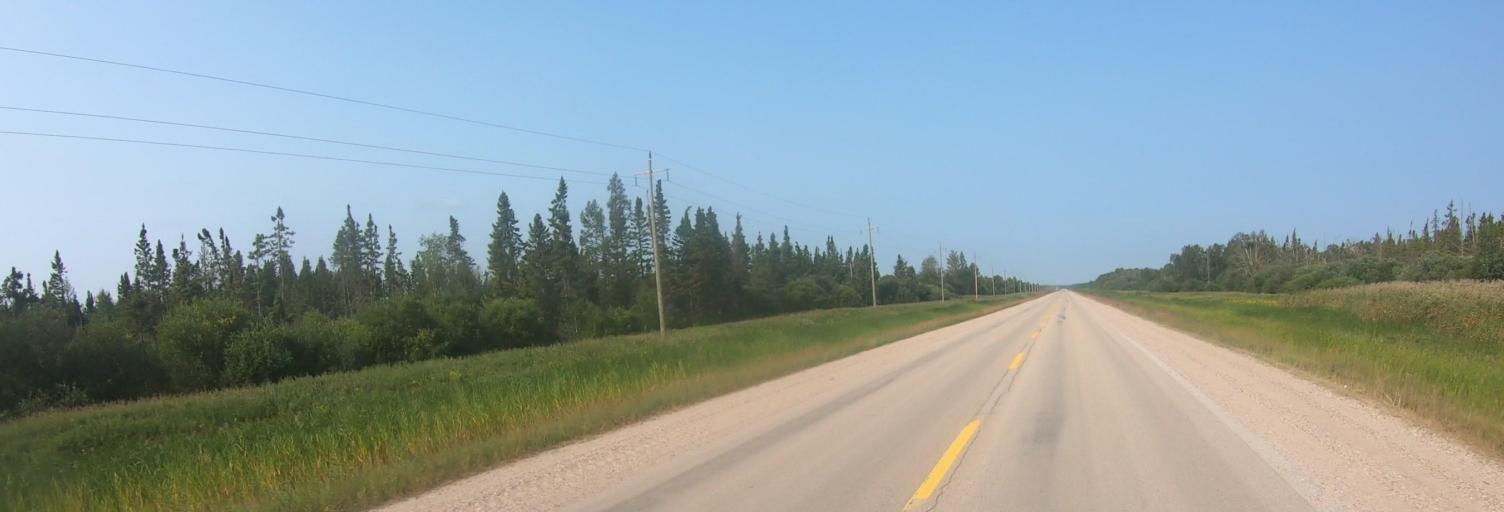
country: US
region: Minnesota
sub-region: Roseau County
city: Roseau
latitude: 49.0234
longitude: -95.6729
